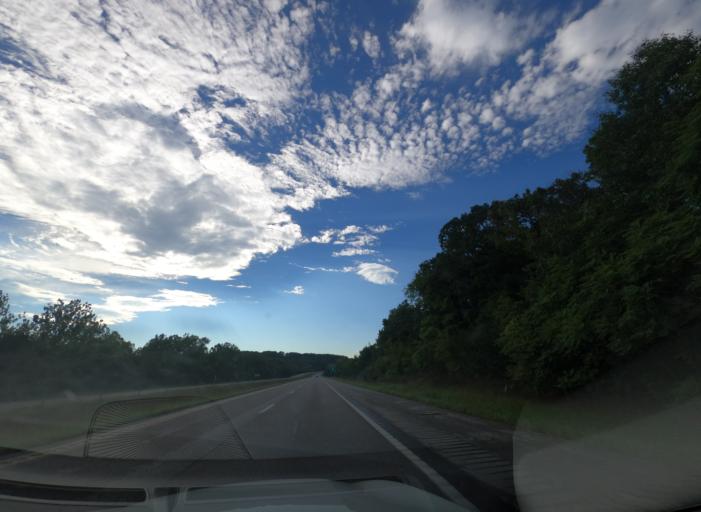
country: US
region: Missouri
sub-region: Jefferson County
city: Crystal City
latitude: 38.1477
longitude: -90.3450
